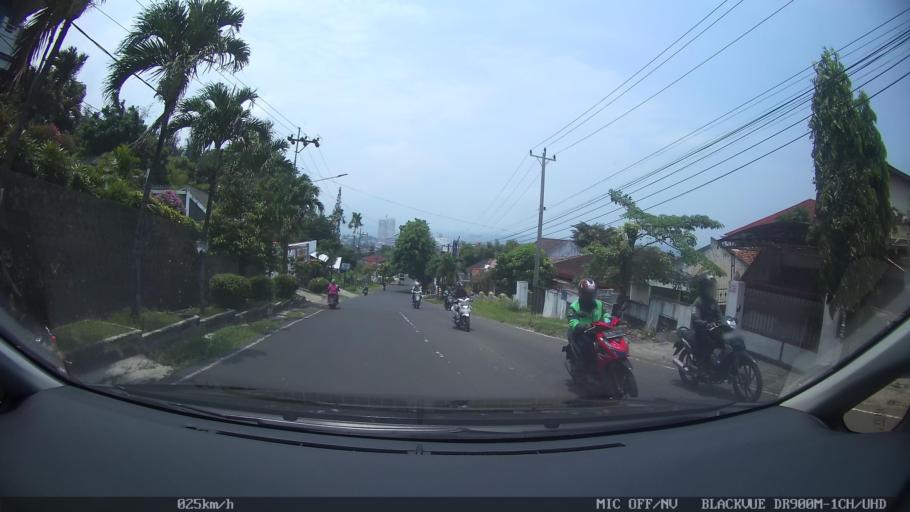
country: ID
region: Lampung
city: Bandarlampung
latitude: -5.4315
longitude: 105.2719
